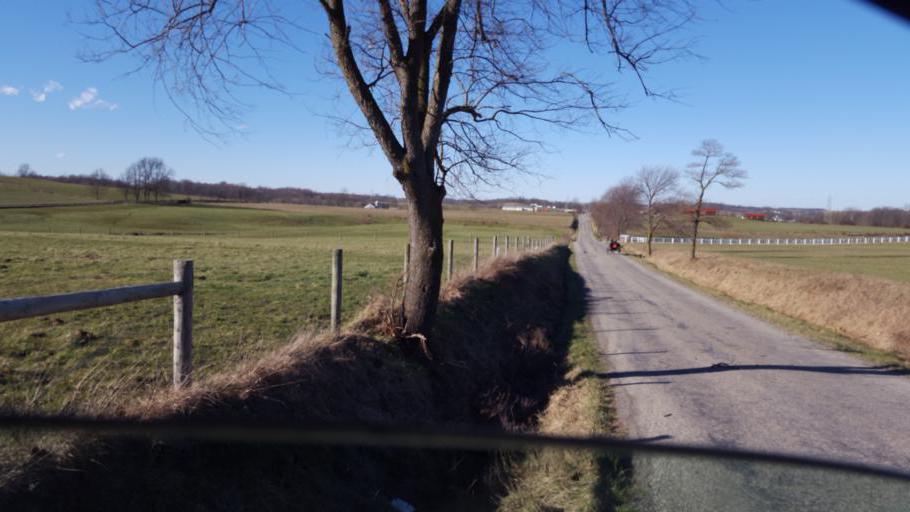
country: US
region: Ohio
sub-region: Tuscarawas County
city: Sugarcreek
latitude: 40.5984
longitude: -81.7614
